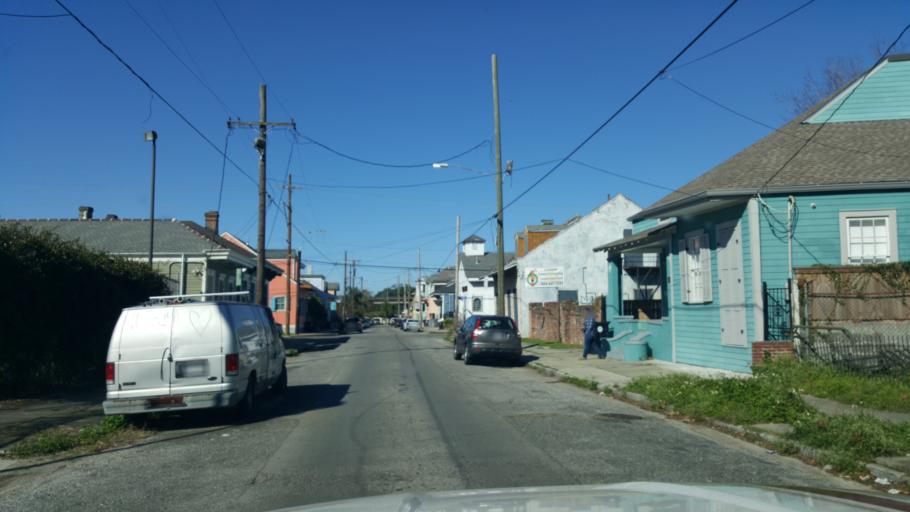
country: US
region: Louisiana
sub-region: Orleans Parish
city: New Orleans
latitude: 29.9657
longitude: -90.0683
